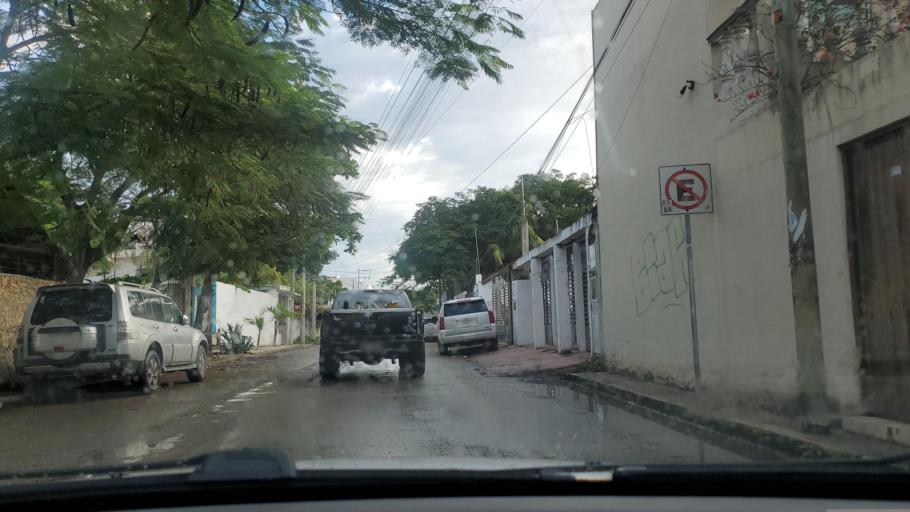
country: MX
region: Quintana Roo
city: Tulum
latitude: 20.2106
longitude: -87.4670
